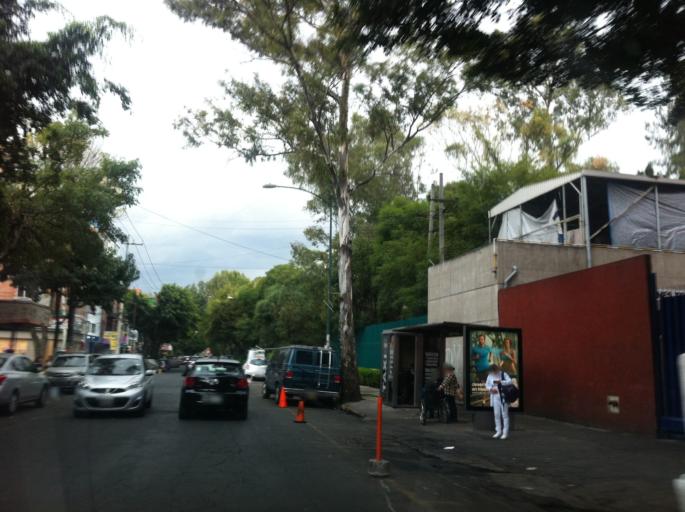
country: MX
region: Mexico City
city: Benito Juarez
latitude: 19.4105
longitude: -99.1507
